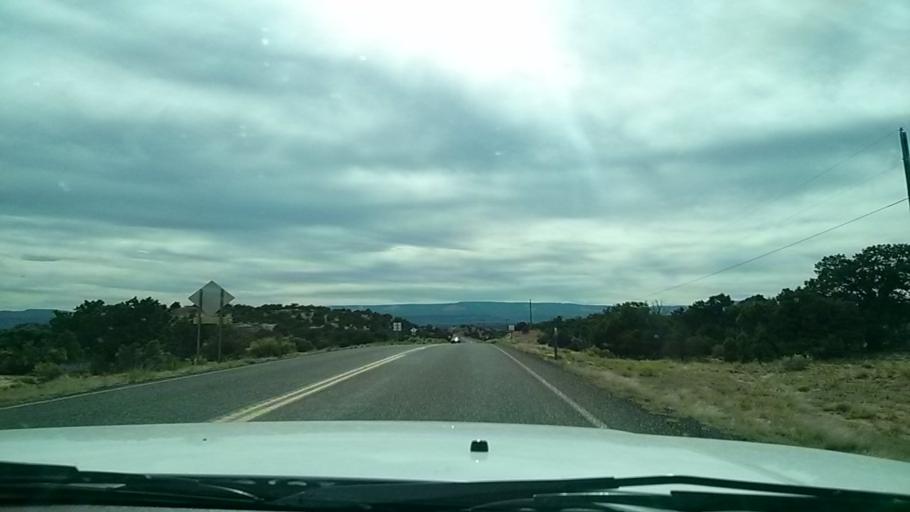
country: US
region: Utah
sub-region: Wayne County
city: Loa
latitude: 37.7505
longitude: -111.4578
